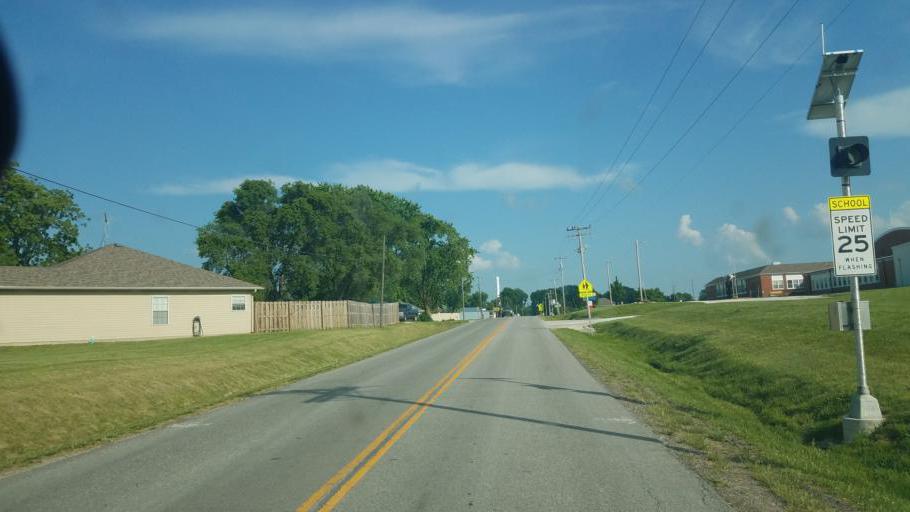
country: US
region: Missouri
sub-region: Moniteau County
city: California
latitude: 38.8167
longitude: -92.5948
